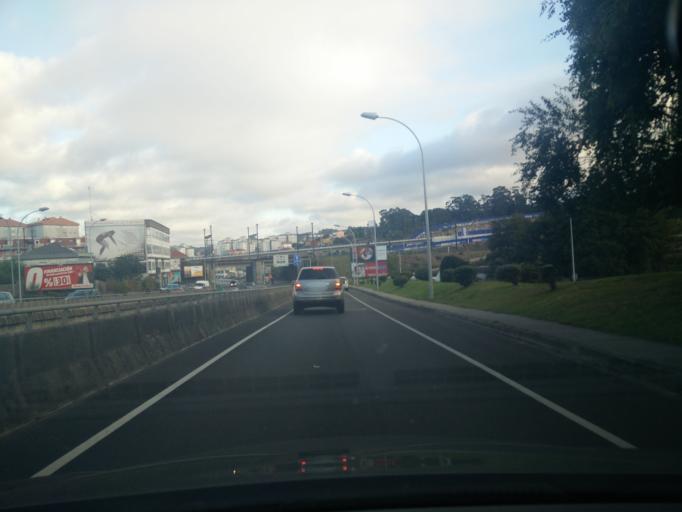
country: ES
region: Galicia
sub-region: Provincia da Coruna
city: A Coruna
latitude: 43.3477
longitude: -8.4198
